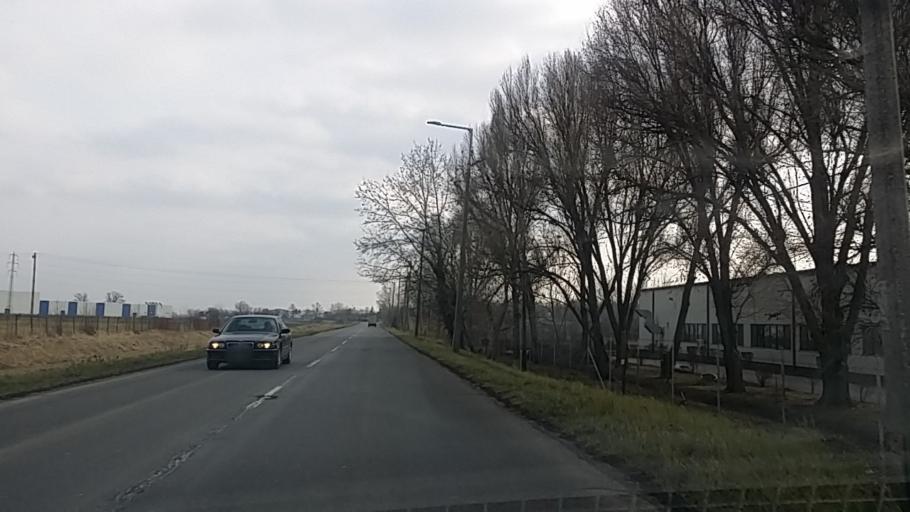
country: HU
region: Tolna
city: Szekszard
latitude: 46.3490
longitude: 18.7242
